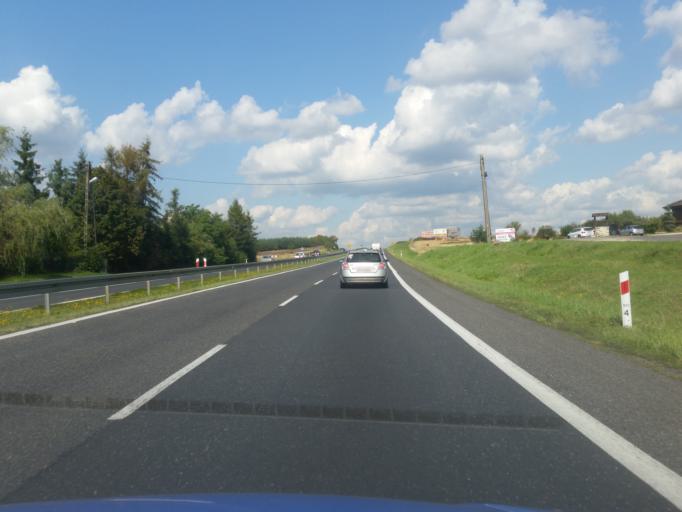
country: PL
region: Silesian Voivodeship
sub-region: Powiat myszkowski
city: Kozieglowy
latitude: 50.5774
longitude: 19.1631
